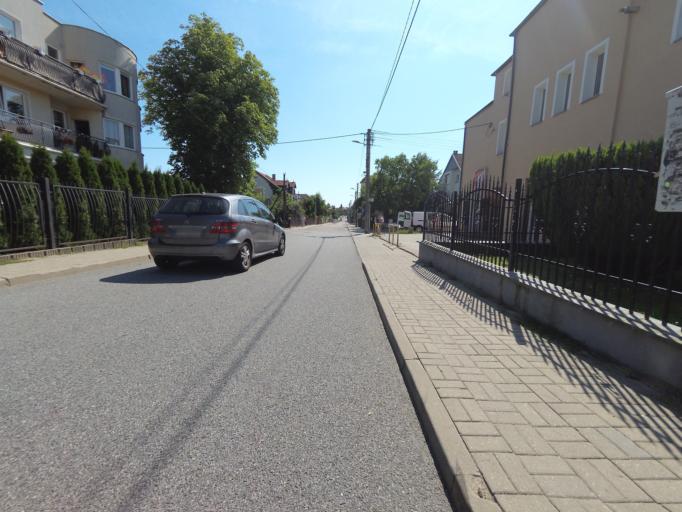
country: PL
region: Pomeranian Voivodeship
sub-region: Gdynia
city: Gdynia
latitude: 54.4946
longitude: 18.5110
